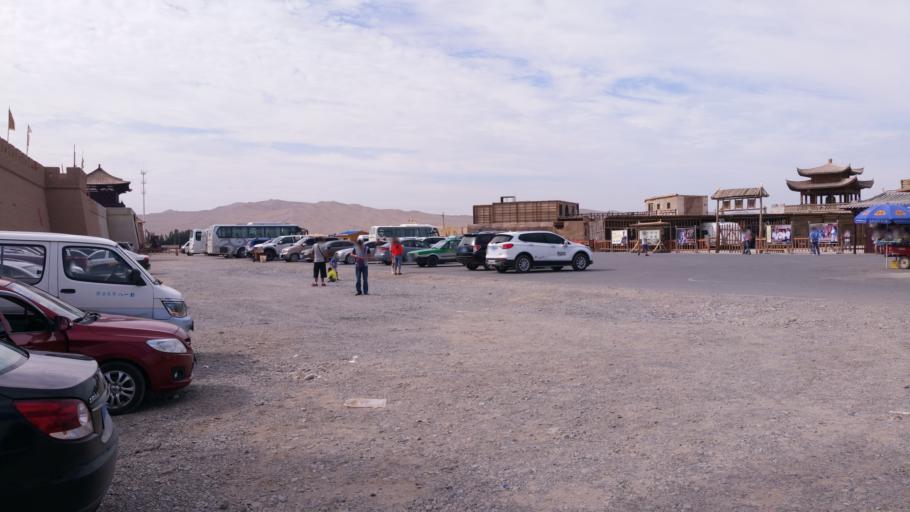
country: CN
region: Gansu Sheng
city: Qili
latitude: 40.0579
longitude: 94.5160
